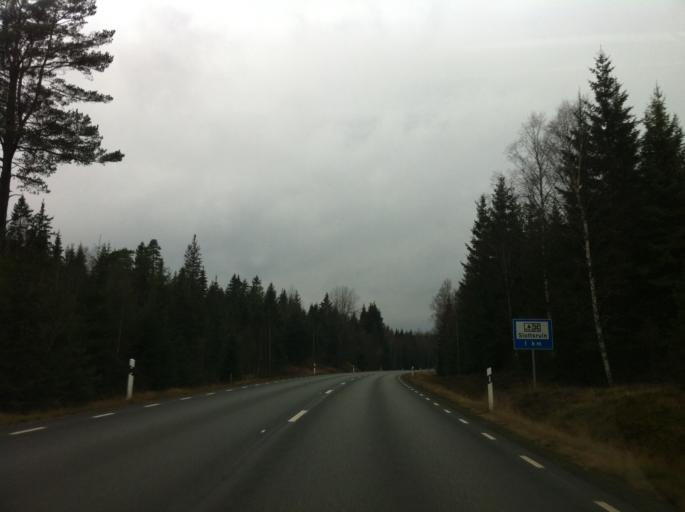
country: SE
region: Joenkoeping
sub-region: Savsjo Kommun
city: Saevsjoe
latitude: 57.3921
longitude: 14.7313
